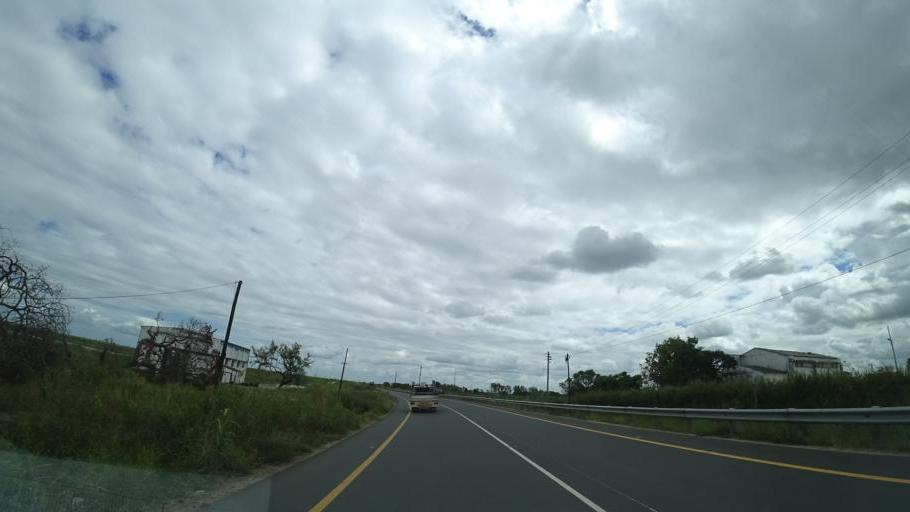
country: MZ
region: Sofala
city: Dondo
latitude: -19.4958
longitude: 34.5921
